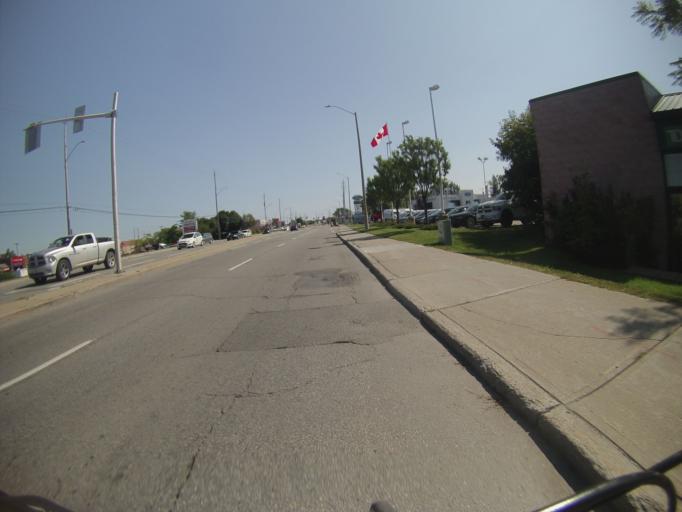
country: CA
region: Ontario
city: Ottawa
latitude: 45.3537
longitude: -75.6456
